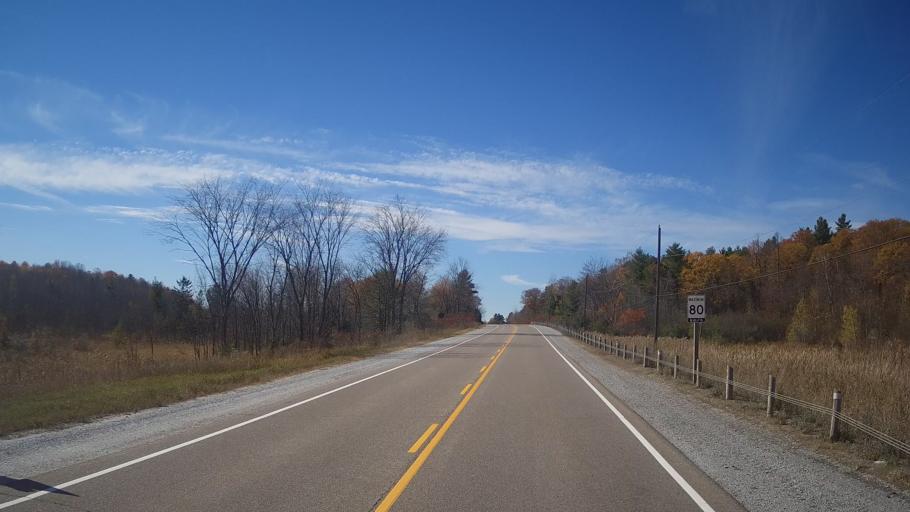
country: CA
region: Ontario
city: Perth
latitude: 44.8398
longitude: -76.5082
